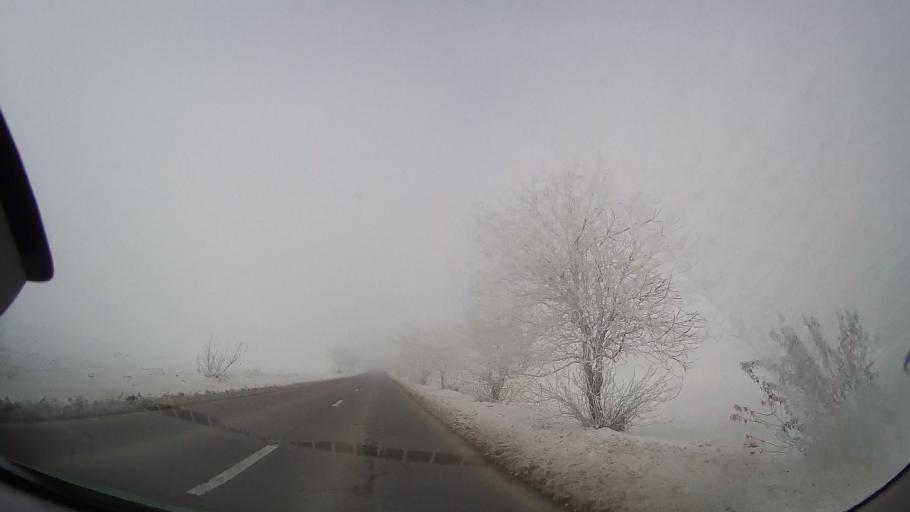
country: RO
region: Iasi
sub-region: Comuna Stolniceni-Prajescu
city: Stolniceni-Prajescu
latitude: 47.1849
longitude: 26.7417
